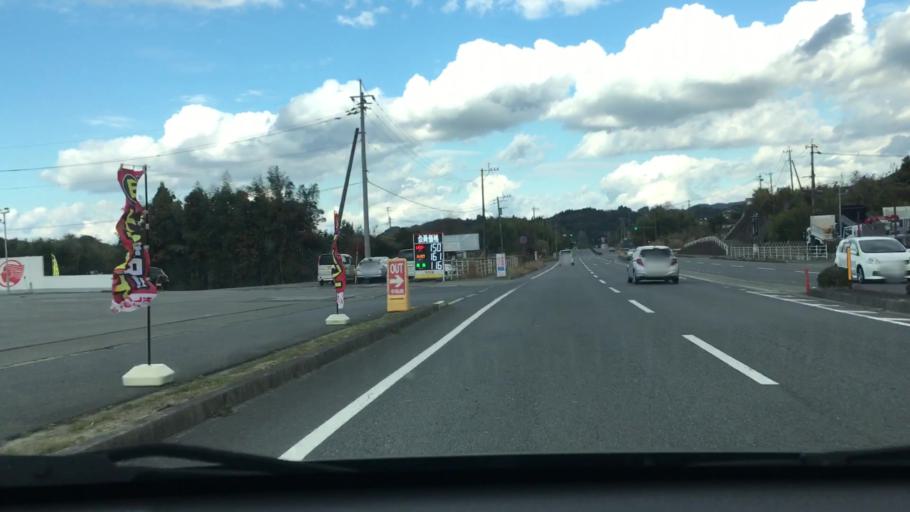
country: JP
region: Oita
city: Oita
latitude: 33.1253
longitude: 131.6553
